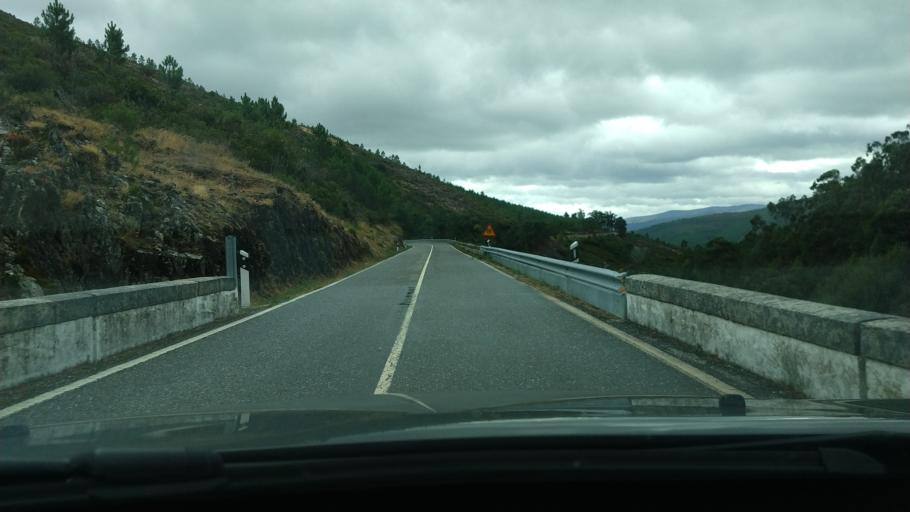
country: PT
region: Guarda
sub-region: Seia
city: Seia
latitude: 40.2494
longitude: -7.6715
